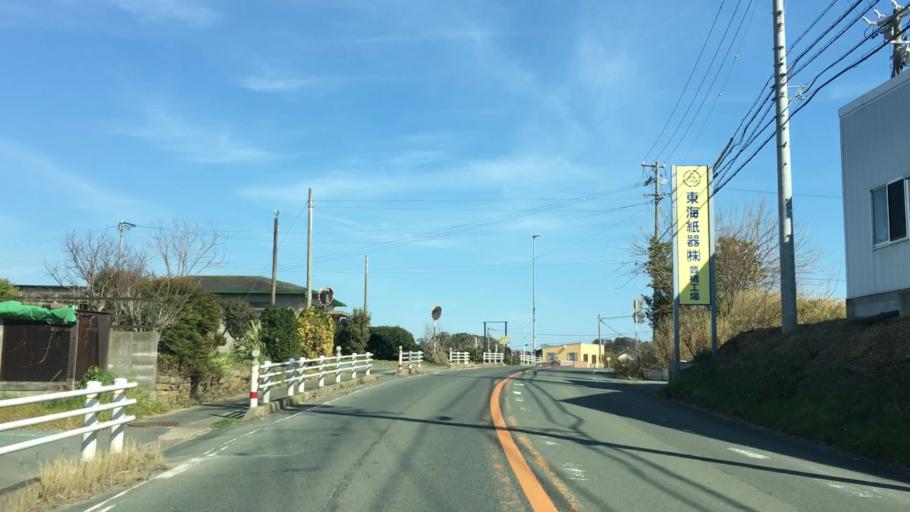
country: JP
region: Shizuoka
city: Kosai-shi
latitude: 34.6851
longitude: 137.4724
